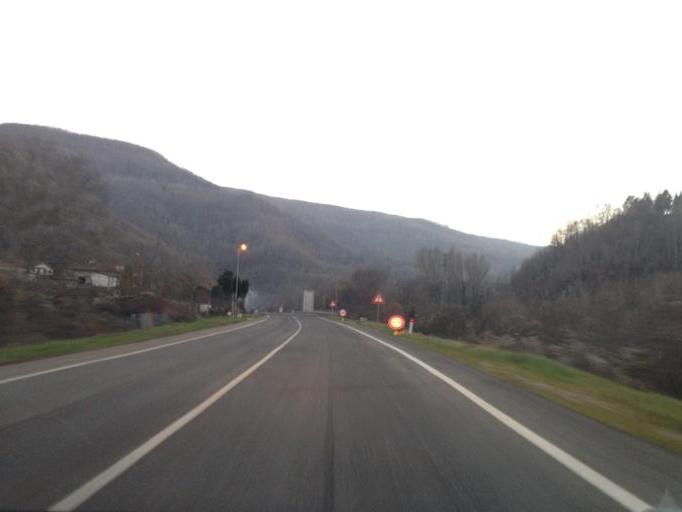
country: IT
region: Latium
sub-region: Provincia di Rieti
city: Accumoli
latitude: 42.7352
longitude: 13.2659
